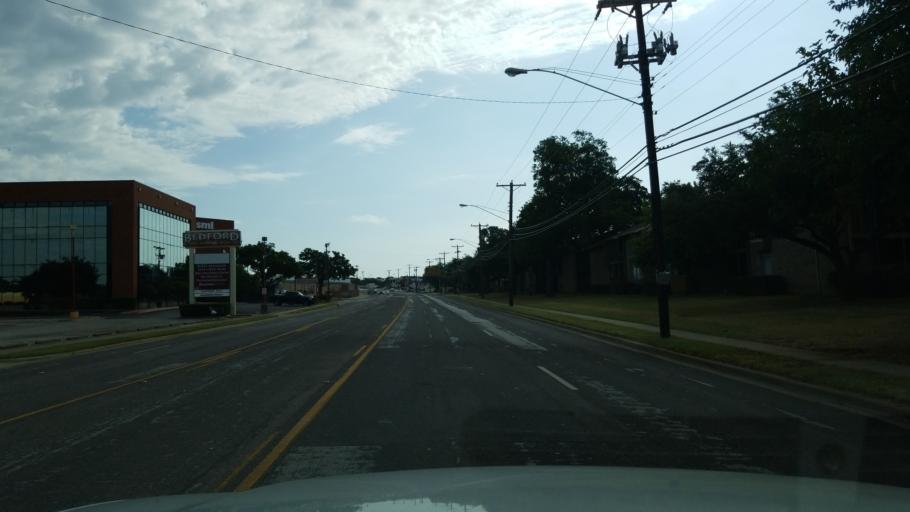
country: US
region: Texas
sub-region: Tarrant County
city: Hurst
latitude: 32.8340
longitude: -97.1653
